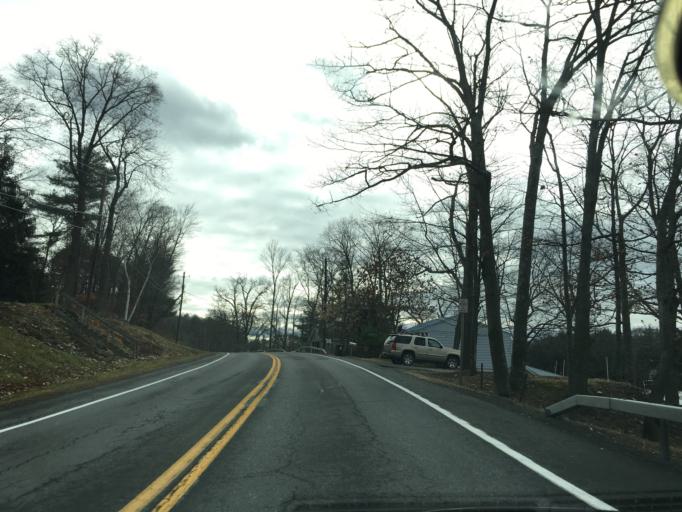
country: US
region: New York
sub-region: Rensselaer County
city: Averill Park
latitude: 42.6118
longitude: -73.5238
